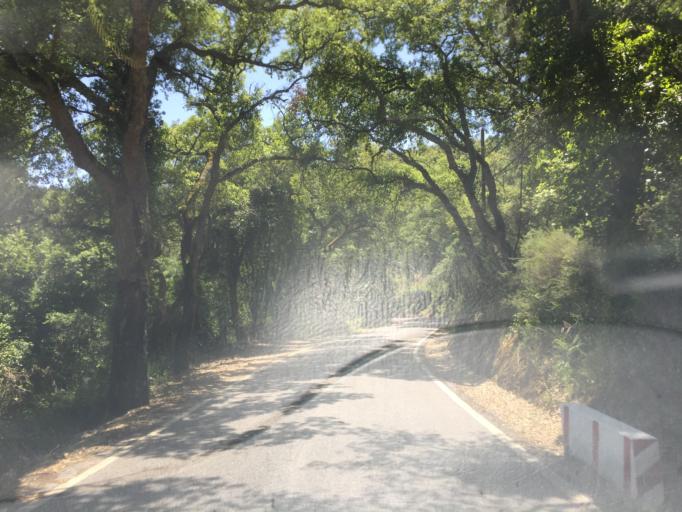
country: PT
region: Lisbon
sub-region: Mafra
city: Venda do Pinheiro
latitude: 38.8912
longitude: -9.2166
